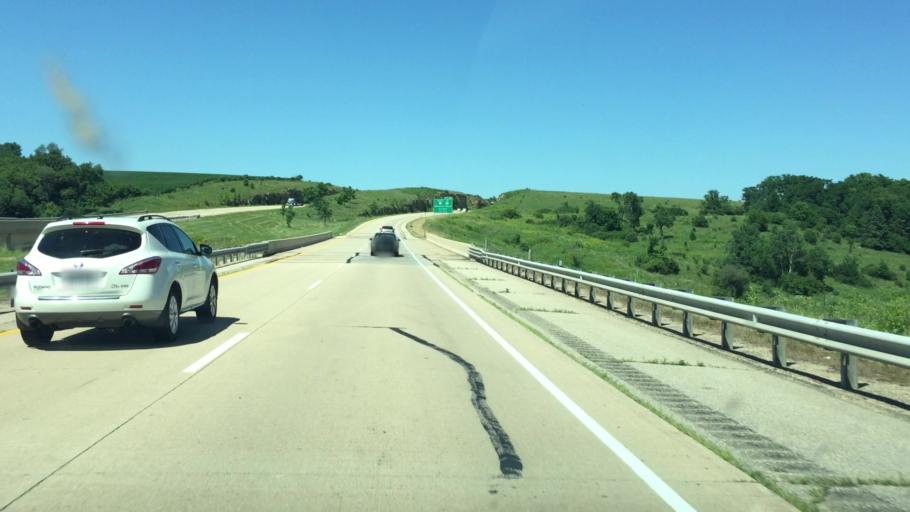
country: US
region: Wisconsin
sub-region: Iowa County
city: Mineral Point
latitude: 42.8714
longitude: -90.1928
